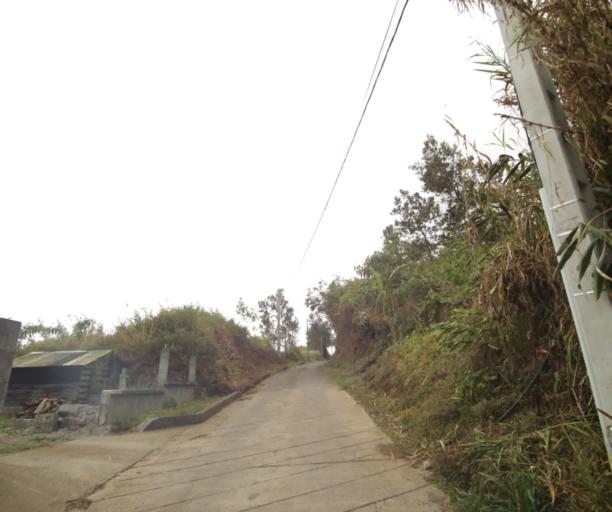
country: RE
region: Reunion
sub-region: Reunion
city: Saint-Paul
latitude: -21.0087
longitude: 55.3454
